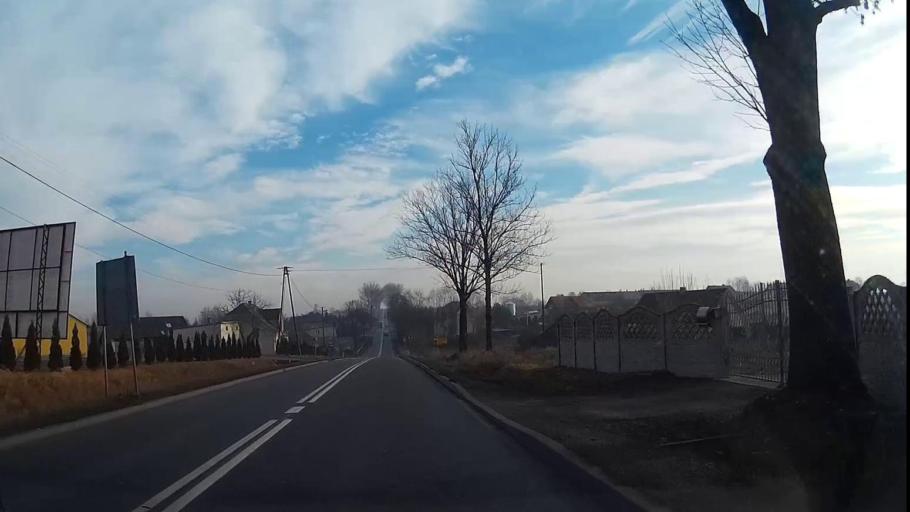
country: PL
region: Lesser Poland Voivodeship
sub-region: Powiat krakowski
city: Czulow
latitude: 50.0380
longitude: 19.6808
